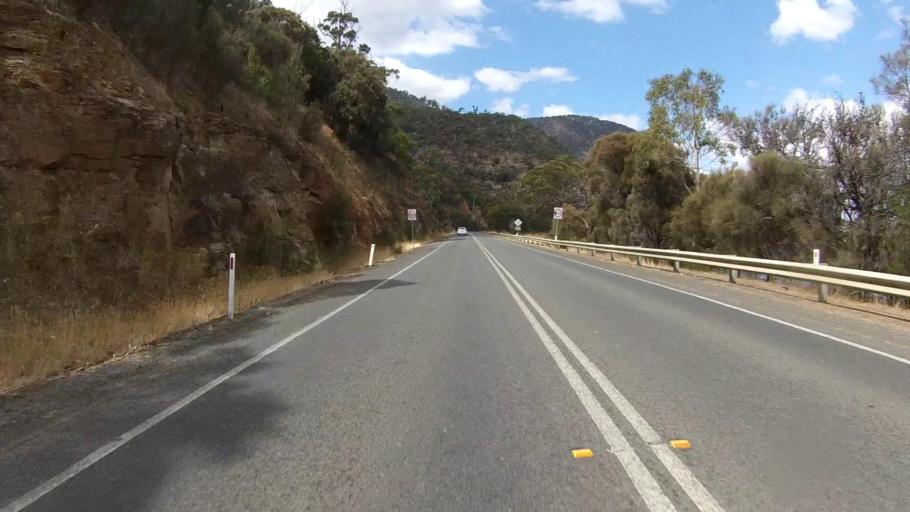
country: AU
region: Tasmania
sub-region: Brighton
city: Old Beach
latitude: -42.7845
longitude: 147.2885
